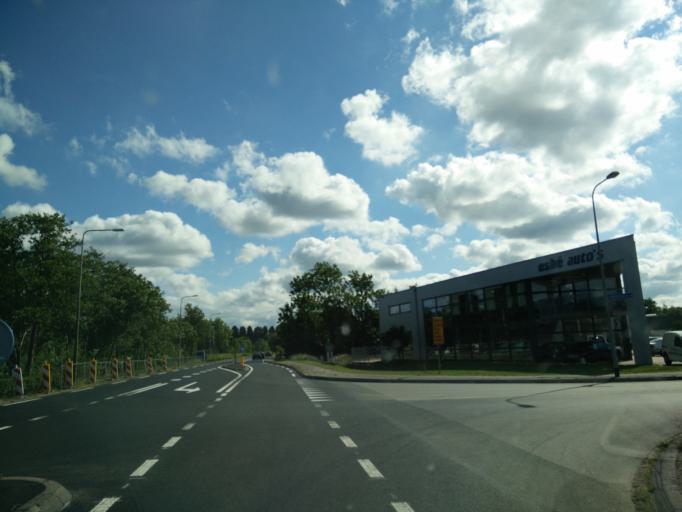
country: NL
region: Groningen
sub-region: Gemeente Groningen
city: Korrewegwijk
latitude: 53.2456
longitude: 6.5761
